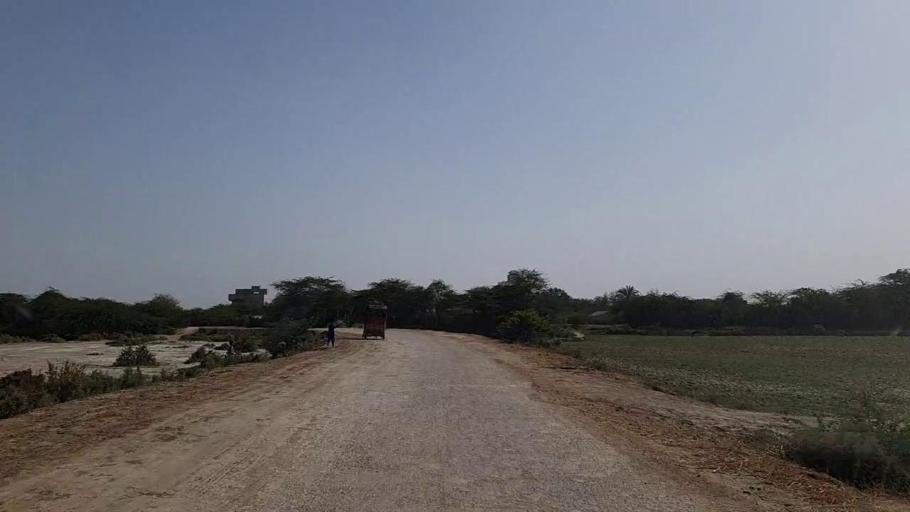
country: PK
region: Sindh
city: Jati
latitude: 24.3578
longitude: 68.2731
